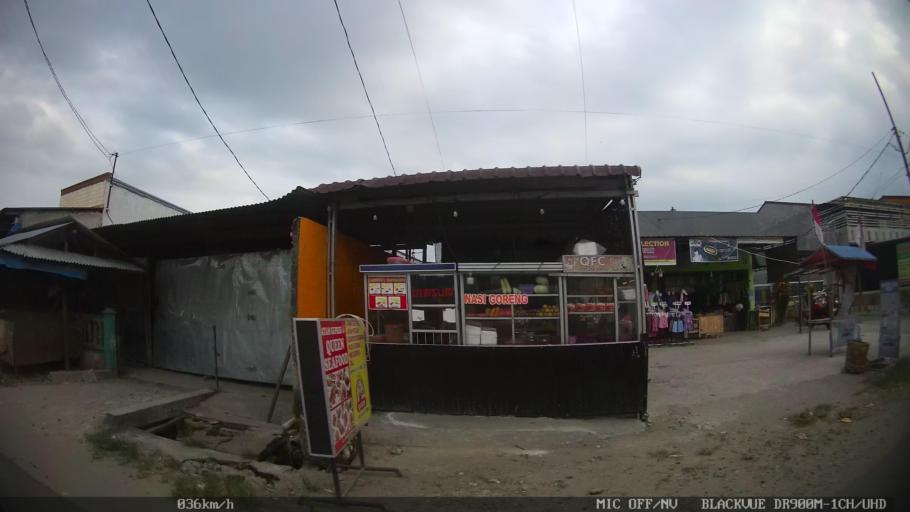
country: ID
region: North Sumatra
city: Sunggal
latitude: 3.5582
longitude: 98.5531
